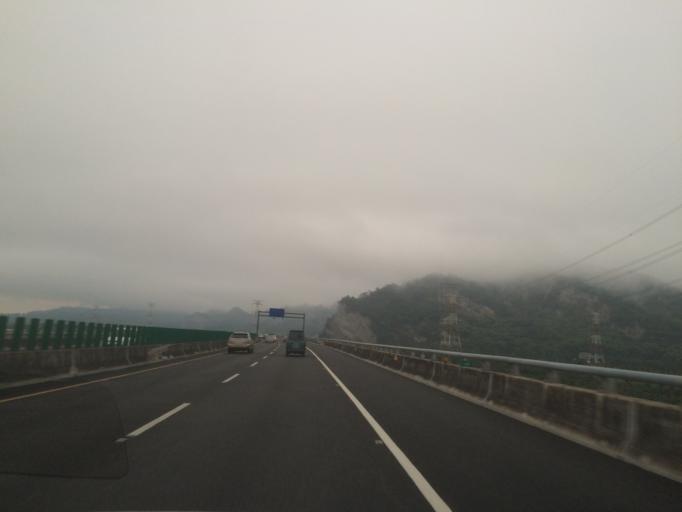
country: TW
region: Taiwan
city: Zhongxing New Village
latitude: 23.9908
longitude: 120.7538
